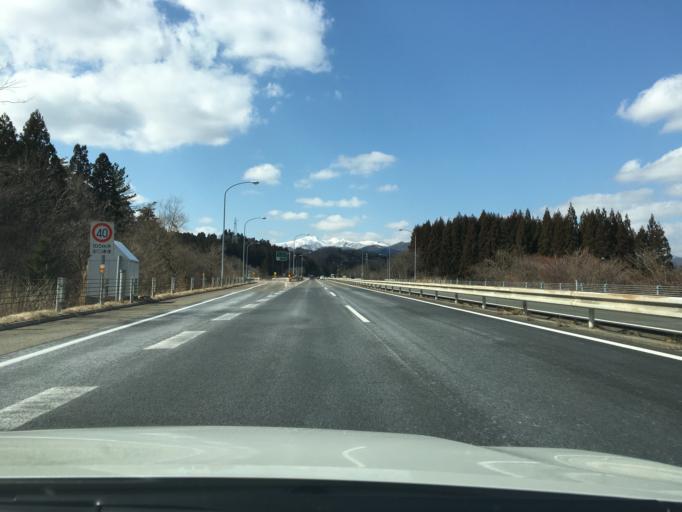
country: JP
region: Miyagi
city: Okawara
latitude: 38.1740
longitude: 140.6249
